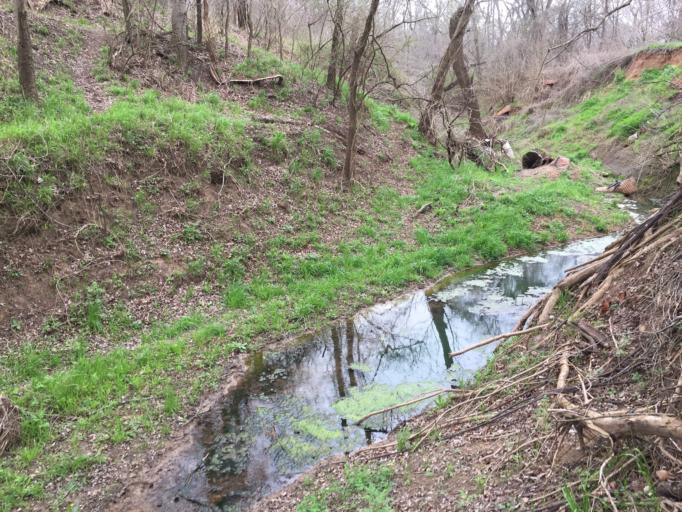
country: US
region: Texas
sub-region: Bastrop County
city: Bastrop
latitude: 30.0817
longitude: -97.3217
